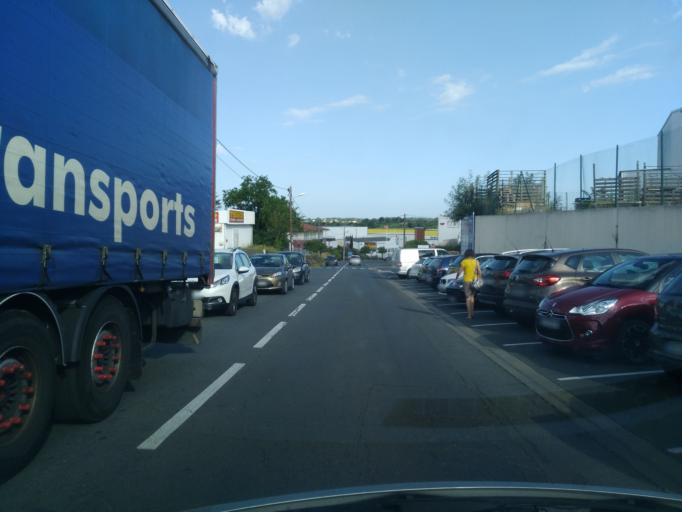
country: FR
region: Poitou-Charentes
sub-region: Departement de la Charente-Maritime
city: Saint-Georges-de-Didonne
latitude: 45.6299
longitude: -0.9944
